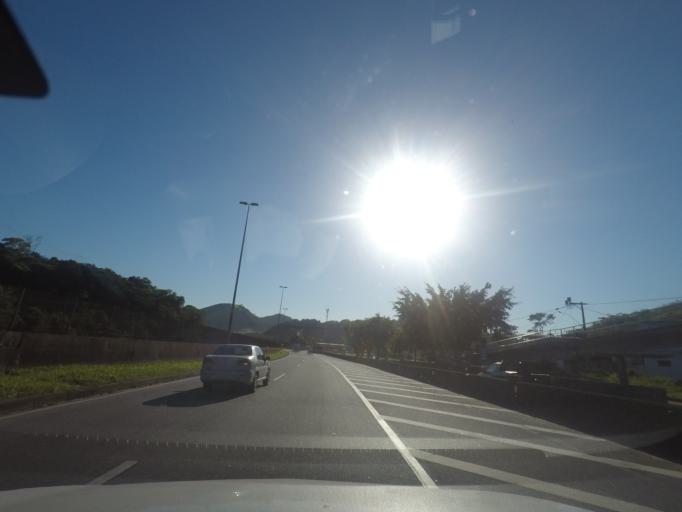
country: BR
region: Rio de Janeiro
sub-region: Petropolis
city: Petropolis
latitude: -22.6575
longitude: -43.1319
